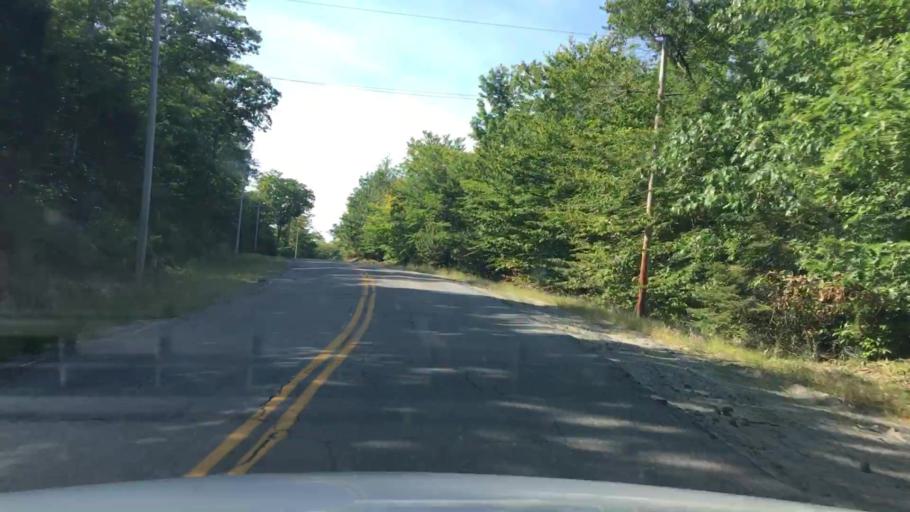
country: US
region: Maine
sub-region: Penobscot County
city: Enfield
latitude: 45.2247
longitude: -68.5392
